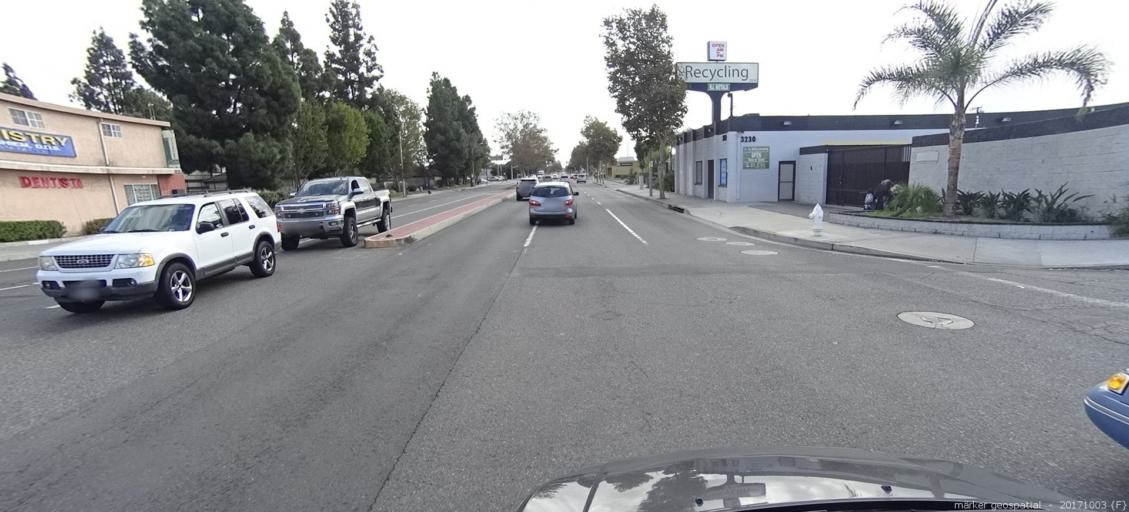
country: US
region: California
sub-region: Orange County
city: Garden Grove
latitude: 33.7598
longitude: -117.9141
